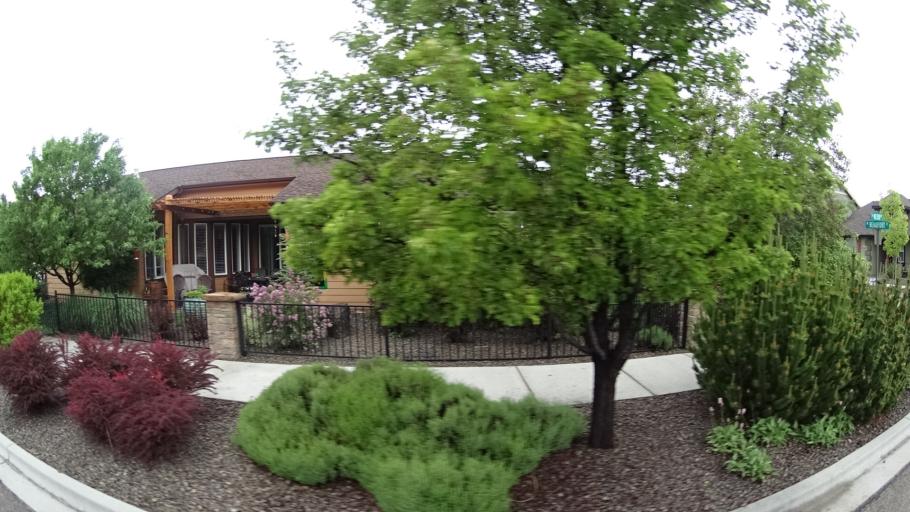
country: US
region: Idaho
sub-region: Ada County
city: Eagle
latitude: 43.7715
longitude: -116.2621
